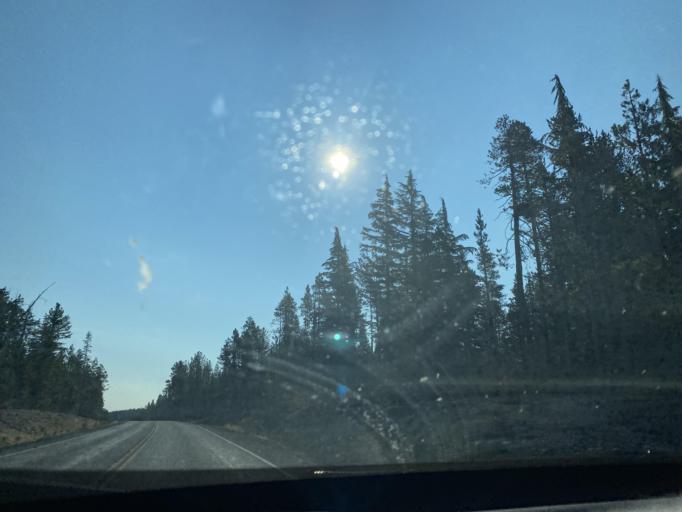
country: US
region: Oregon
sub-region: Deschutes County
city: Three Rivers
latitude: 43.7050
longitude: -121.2489
